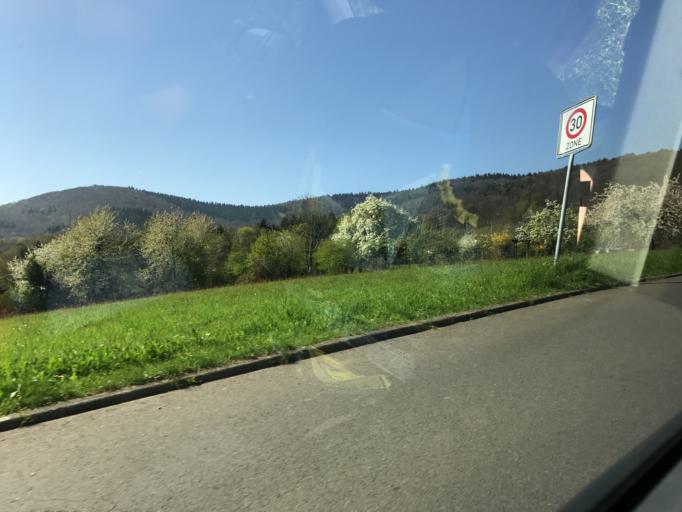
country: DE
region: Baden-Wuerttemberg
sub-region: Karlsruhe Region
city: Wilhelmsfeld
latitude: 49.4214
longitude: 8.7452
